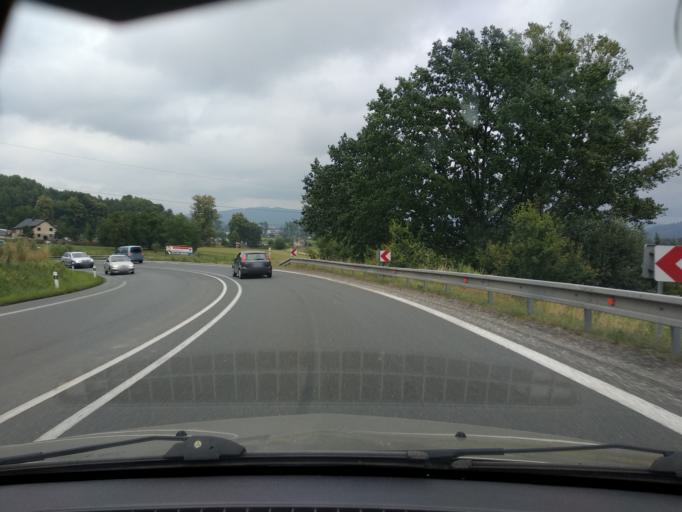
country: CZ
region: Olomoucky
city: Dolni Studenky
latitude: 49.9454
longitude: 16.9533
